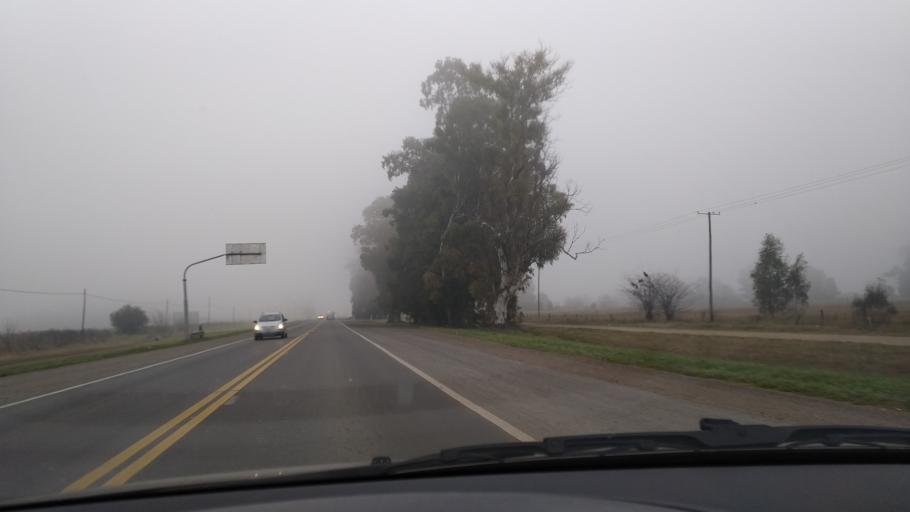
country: AR
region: Buenos Aires
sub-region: Partido de Azul
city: Azul
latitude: -36.7985
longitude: -59.8482
